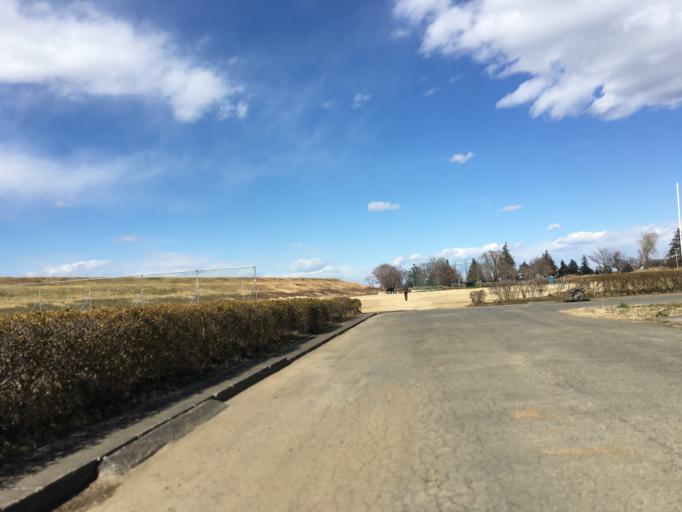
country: JP
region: Saitama
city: Shiki
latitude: 35.8569
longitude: 139.5827
